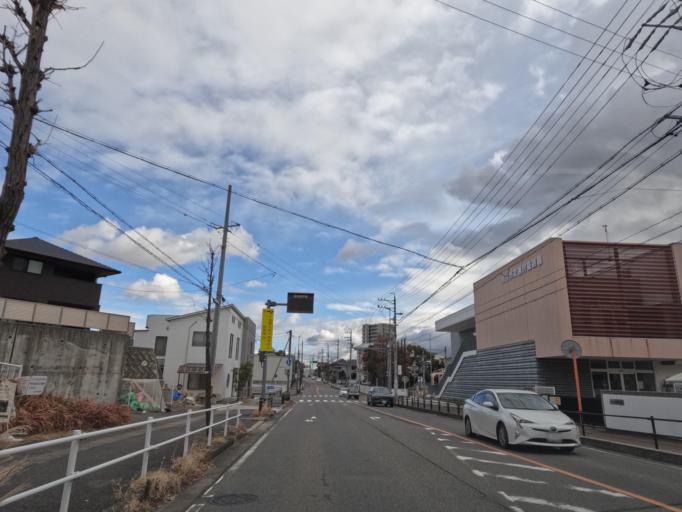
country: JP
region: Aichi
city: Chiryu
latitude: 34.9883
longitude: 137.0141
